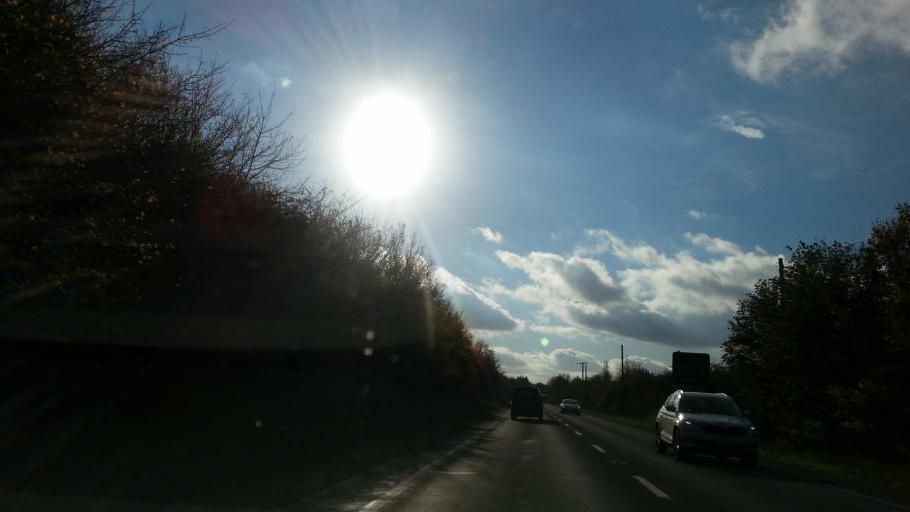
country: GB
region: England
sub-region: Norfolk
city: Harleston
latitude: 52.3795
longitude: 1.2555
